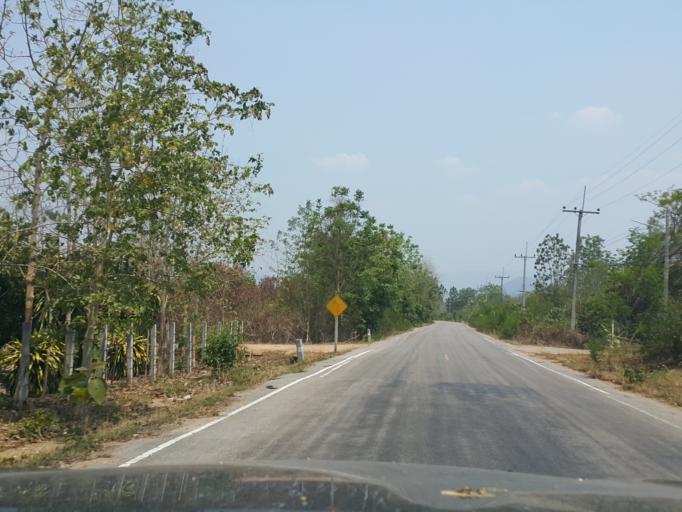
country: TH
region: Lampang
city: Mae Phrik
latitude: 17.5351
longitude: 99.1449
